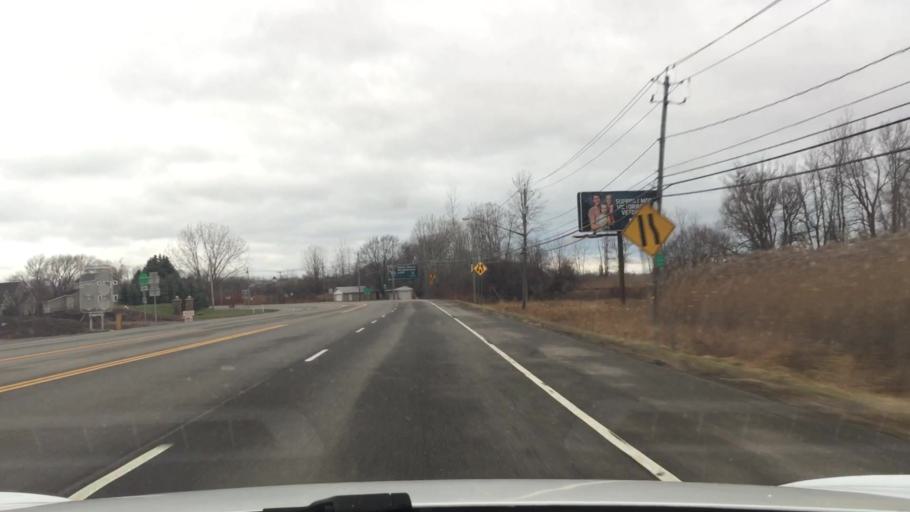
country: US
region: New York
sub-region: Niagara County
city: North Tonawanda
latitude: 43.0579
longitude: -78.9036
